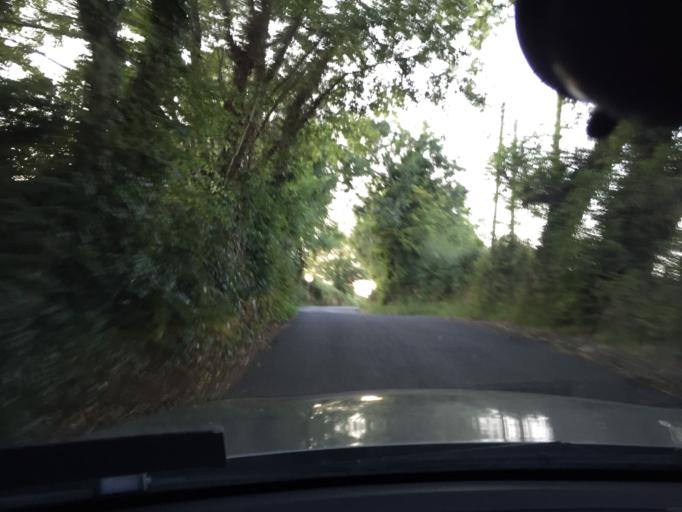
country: IE
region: Leinster
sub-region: Wicklow
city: Enniskerry
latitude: 53.1973
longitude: -6.1962
